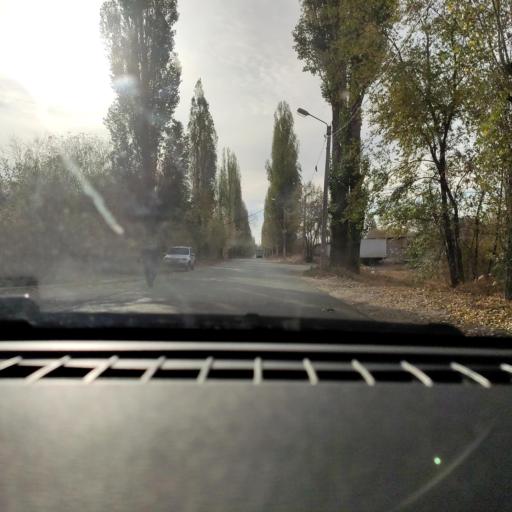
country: RU
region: Voronezj
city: Novaya Usman'
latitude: 51.6456
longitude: 39.3040
